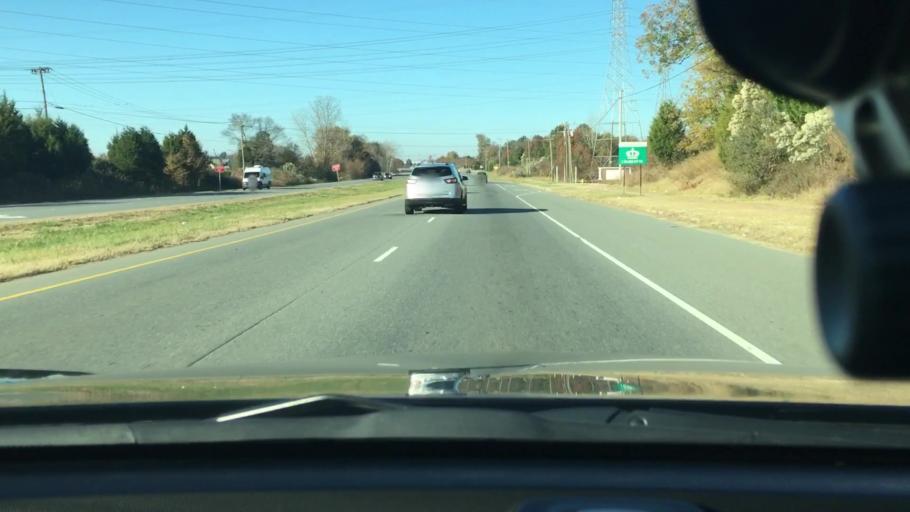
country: US
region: North Carolina
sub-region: Cabarrus County
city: Harrisburg
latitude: 35.3153
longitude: -80.6919
